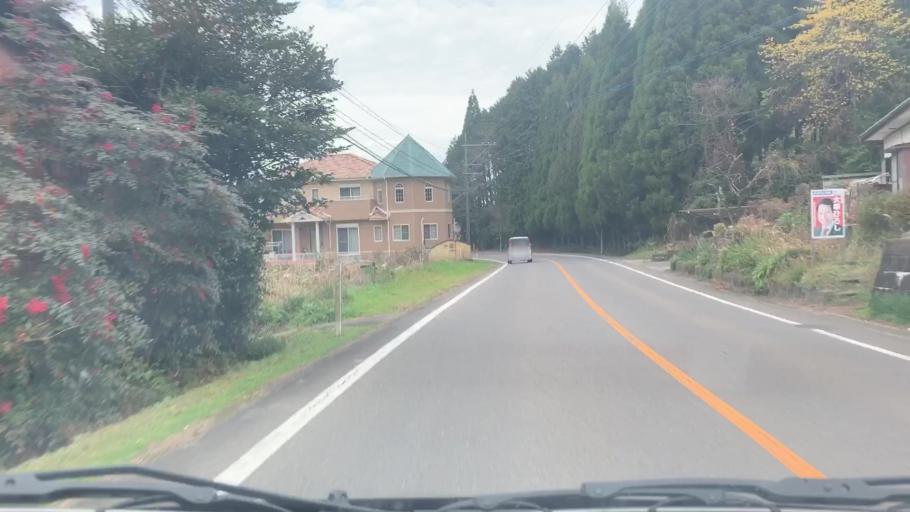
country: JP
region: Saga Prefecture
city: Takeocho-takeo
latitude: 33.1886
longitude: 129.9669
